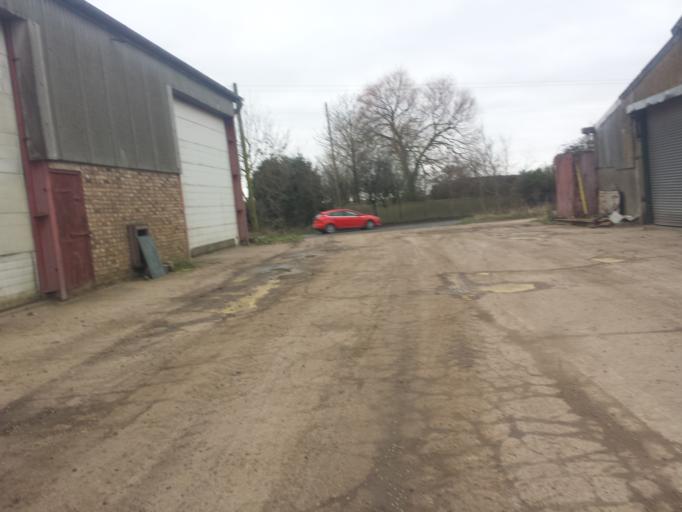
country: GB
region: England
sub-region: Essex
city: Little Clacton
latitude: 51.8865
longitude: 1.1767
